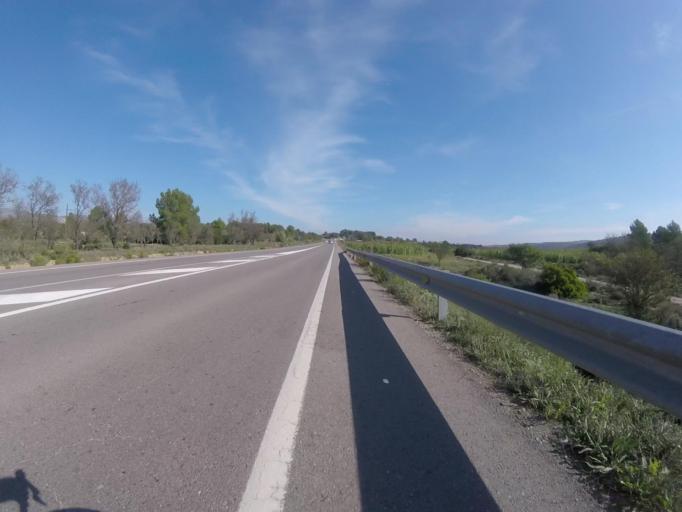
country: ES
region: Valencia
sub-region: Provincia de Castello
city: Benlloch
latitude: 40.2543
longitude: 0.0755
